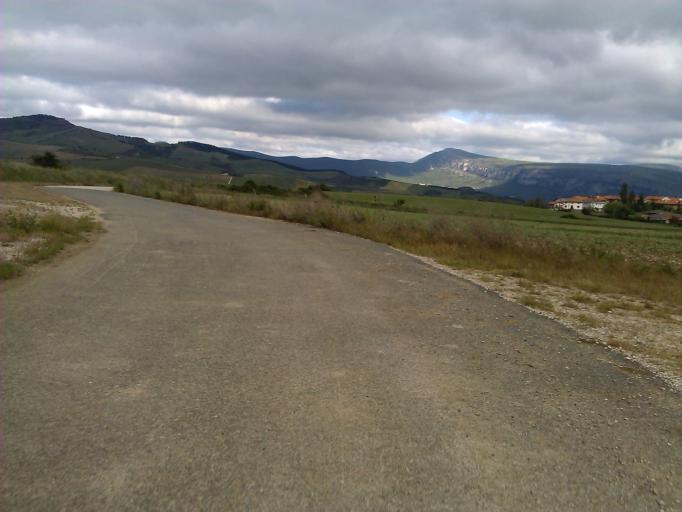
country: ES
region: Navarre
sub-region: Provincia de Navarra
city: Galar
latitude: 42.7520
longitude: -1.7367
